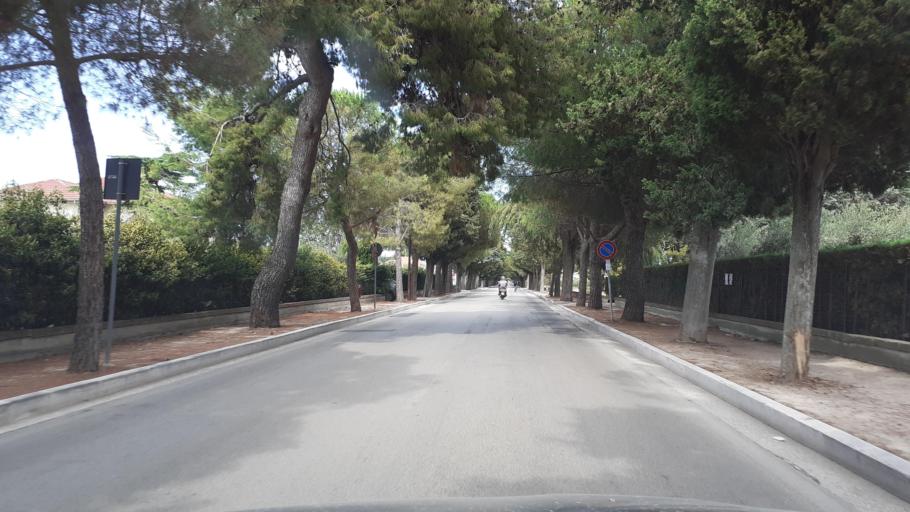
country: IT
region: Abruzzo
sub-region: Provincia di Chieti
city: Fossacesia
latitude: 42.2497
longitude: 14.4887
